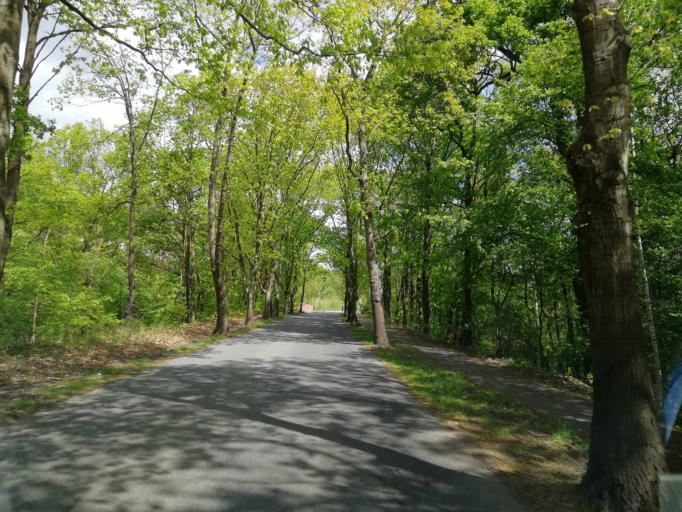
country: DE
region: Brandenburg
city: Lauchhammer
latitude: 51.5097
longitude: 13.8013
